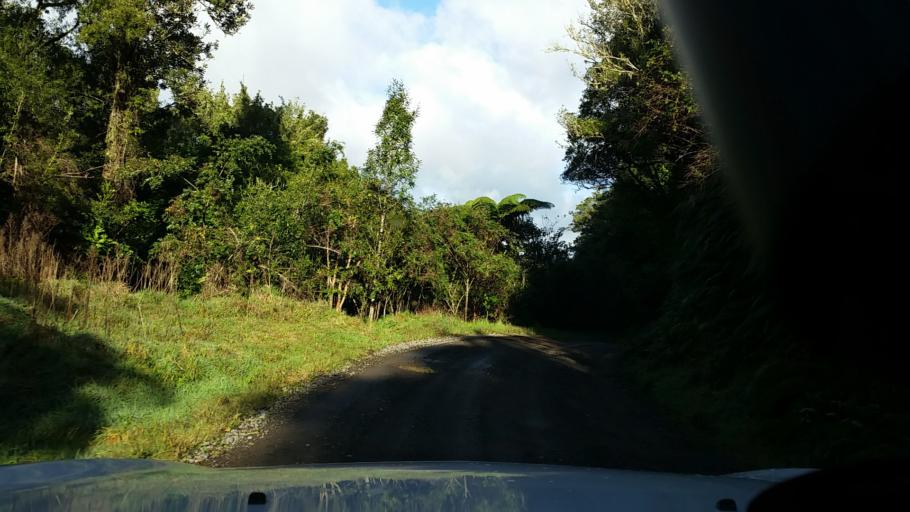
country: NZ
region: Bay of Plenty
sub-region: Kawerau District
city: Kawerau
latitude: -38.0268
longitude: 176.5600
